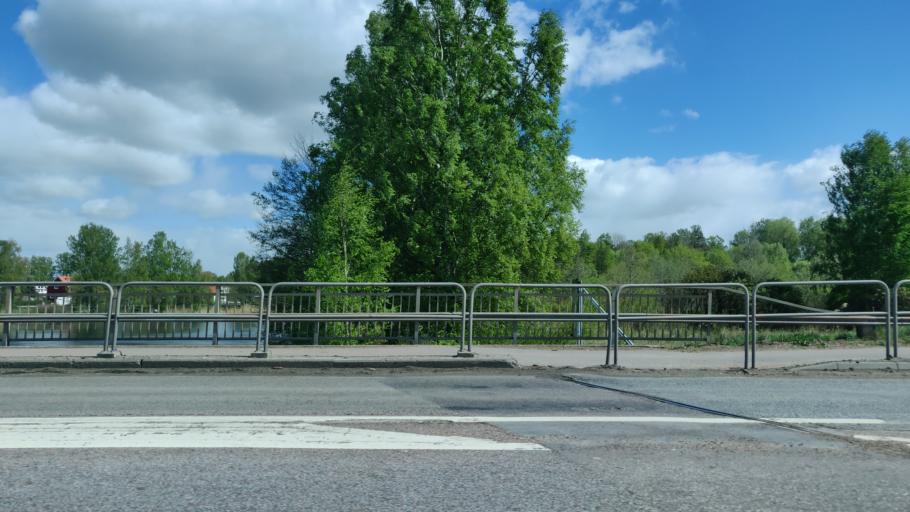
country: SE
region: Vaermland
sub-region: Karlstads Kommun
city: Karlstad
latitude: 59.3856
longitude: 13.5333
